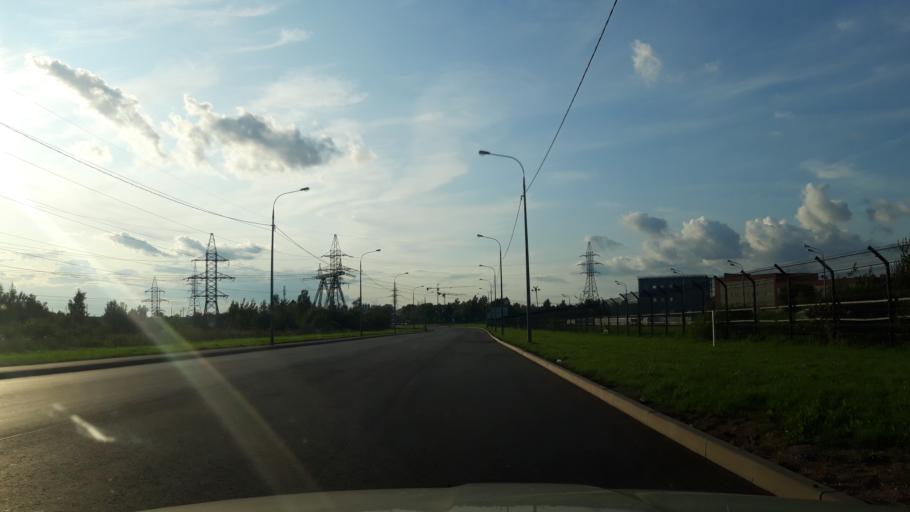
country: RU
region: Moskovskaya
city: Alabushevo
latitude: 55.9993
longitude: 37.1568
